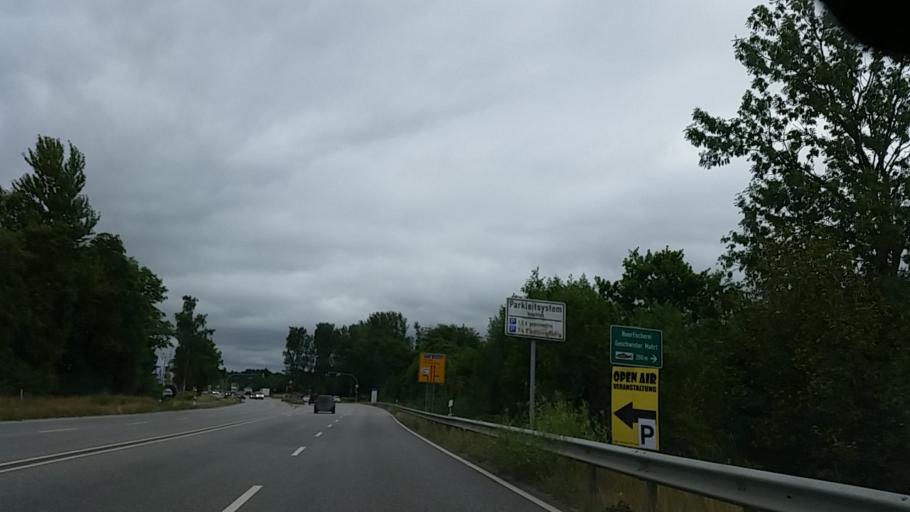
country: DE
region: Schleswig-Holstein
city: Windeby
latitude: 54.4737
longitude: 9.8247
